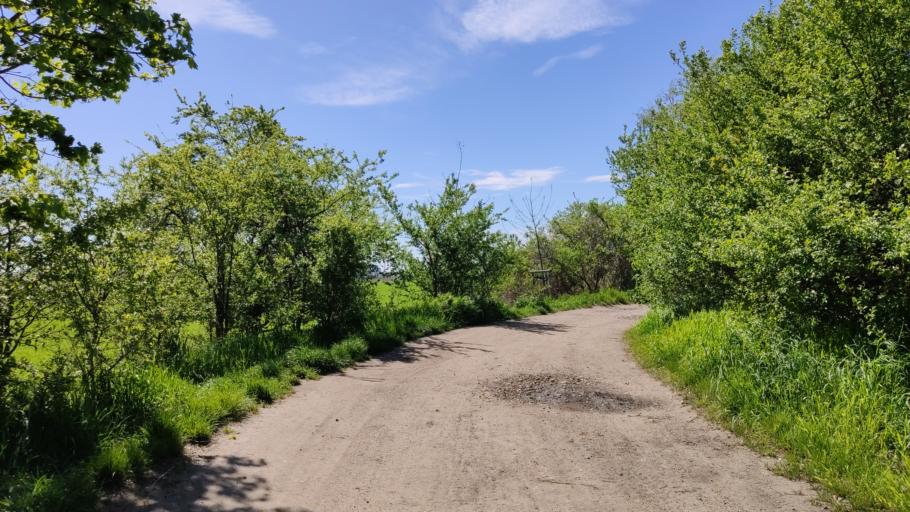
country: PL
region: Lower Silesian Voivodeship
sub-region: Powiat wroclawski
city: Zerniki Wroclawskie
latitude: 51.0597
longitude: 17.0452
